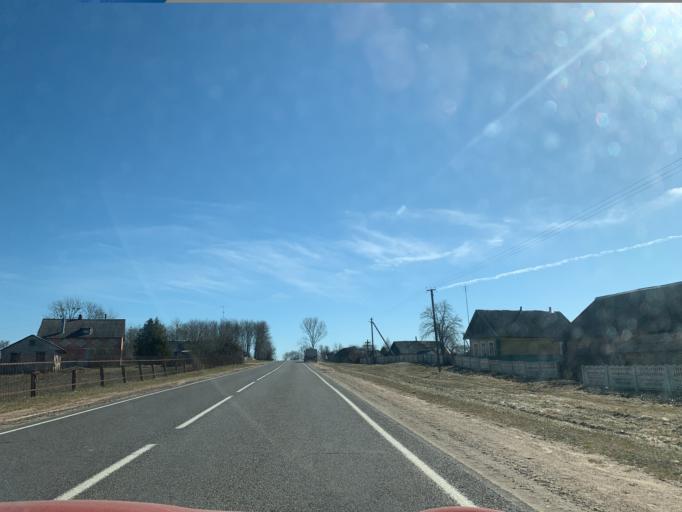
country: BY
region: Minsk
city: Nyasvizh
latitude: 53.2277
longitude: 26.7495
